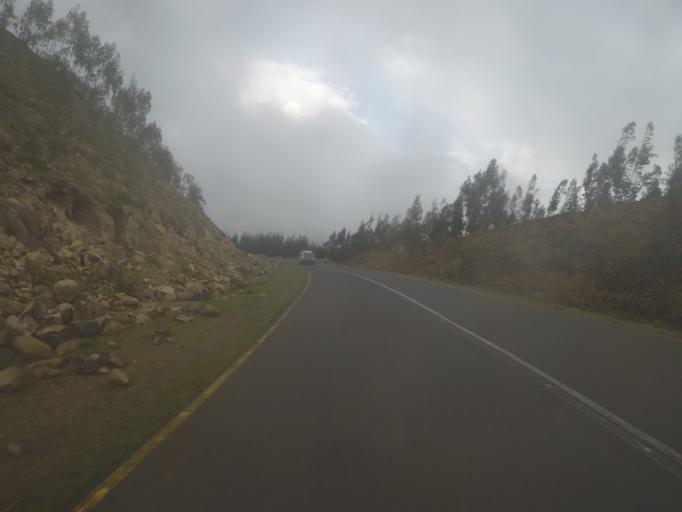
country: ET
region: Amhara
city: Gondar
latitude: 12.7303
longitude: 37.5166
